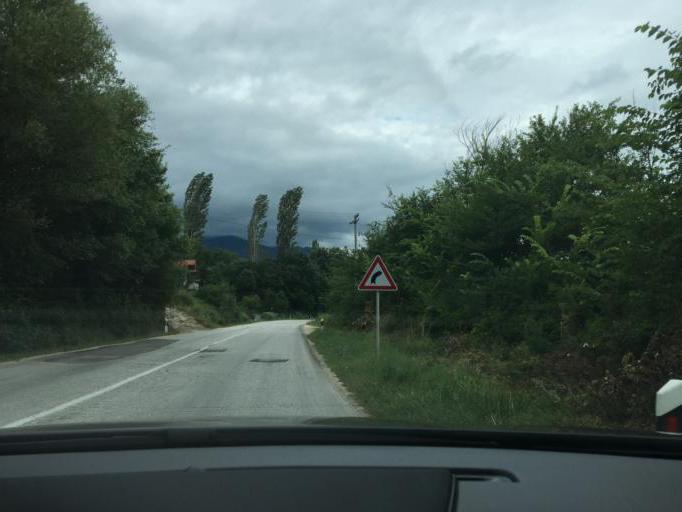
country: MK
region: Kriva Palanka
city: Kriva Palanka
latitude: 42.1778
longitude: 22.2605
